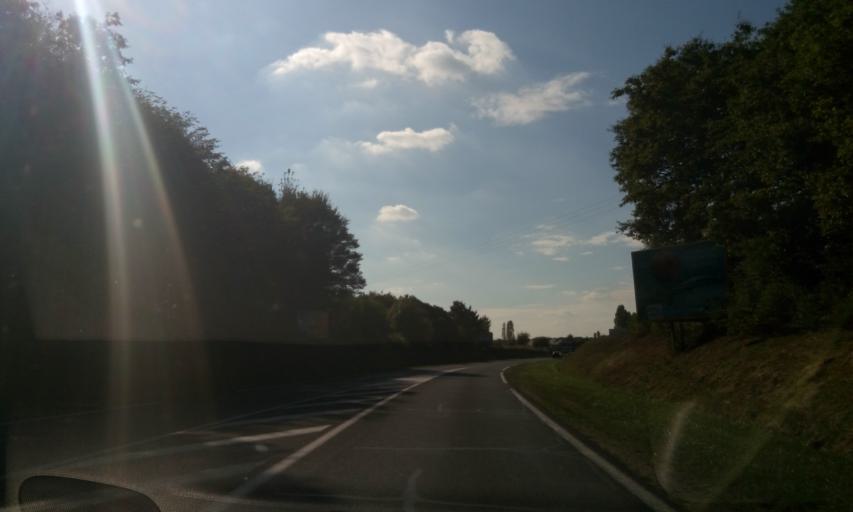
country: FR
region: Centre
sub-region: Departement d'Indre-et-Loire
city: Amboise
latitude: 47.3943
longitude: 1.0150
